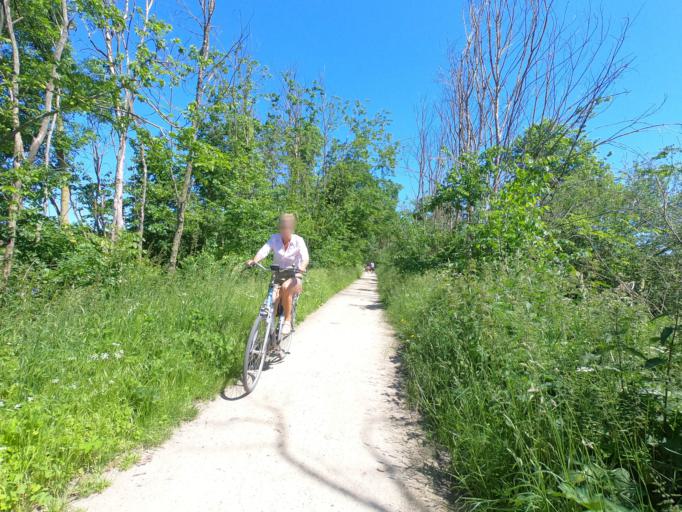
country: BE
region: Flanders
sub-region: Provincie Oost-Vlaanderen
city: Sint-Martens-Latem
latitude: 51.0426
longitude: 3.6616
